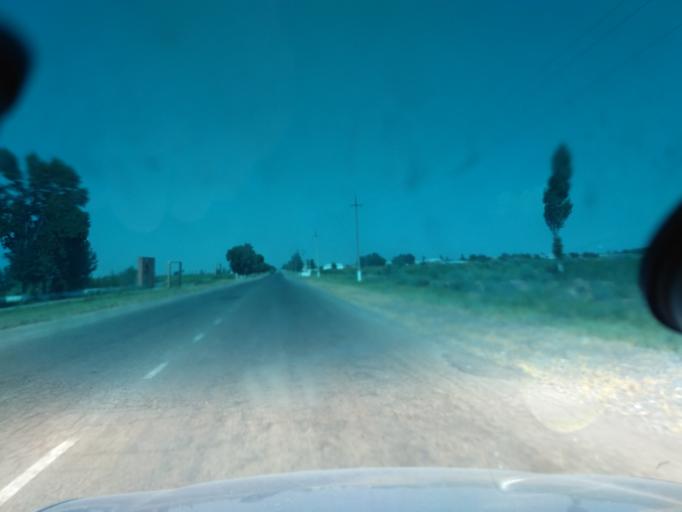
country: UZ
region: Sirdaryo
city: Guliston
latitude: 40.4984
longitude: 68.9393
